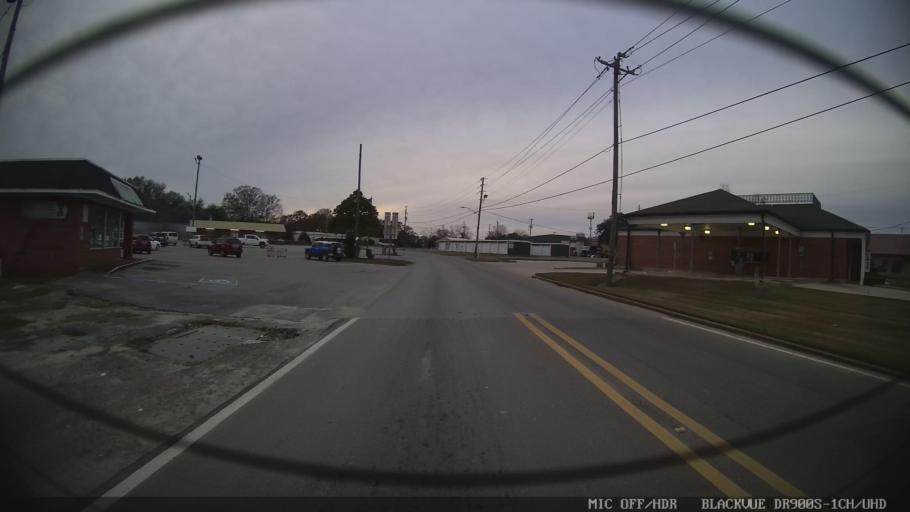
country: US
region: Mississippi
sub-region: Clarke County
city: Quitman
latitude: 32.0381
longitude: -88.7284
